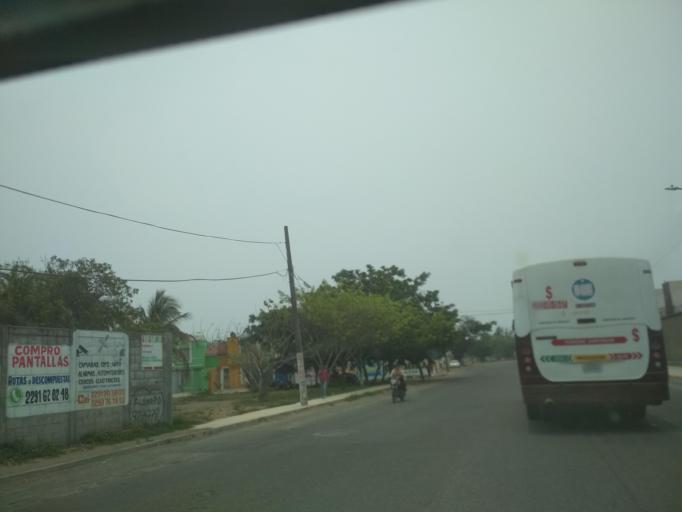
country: MX
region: Veracruz
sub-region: Veracruz
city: Rio Medio [Granja]
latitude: 19.2107
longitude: -96.2052
